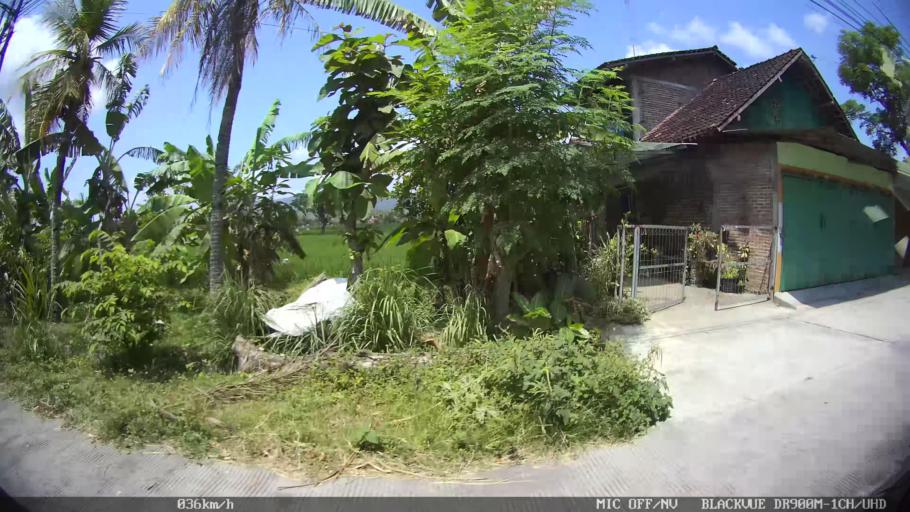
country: ID
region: Daerah Istimewa Yogyakarta
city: Pundong
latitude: -7.9249
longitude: 110.3736
